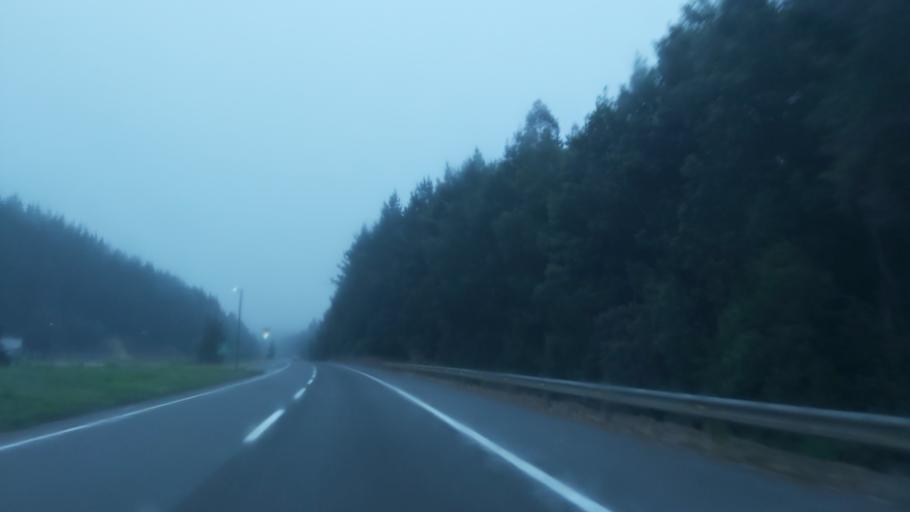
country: CL
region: Biobio
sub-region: Provincia de Concepcion
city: Penco
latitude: -36.7466
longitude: -72.9189
